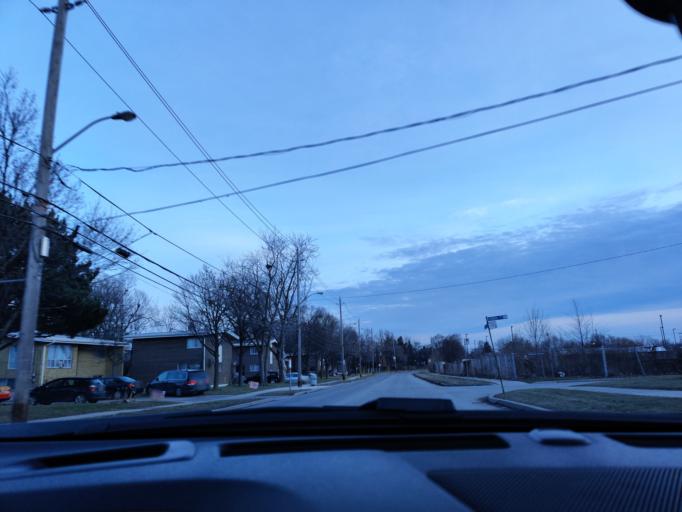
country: CA
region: Ontario
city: Toronto
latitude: 43.7195
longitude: -79.4396
